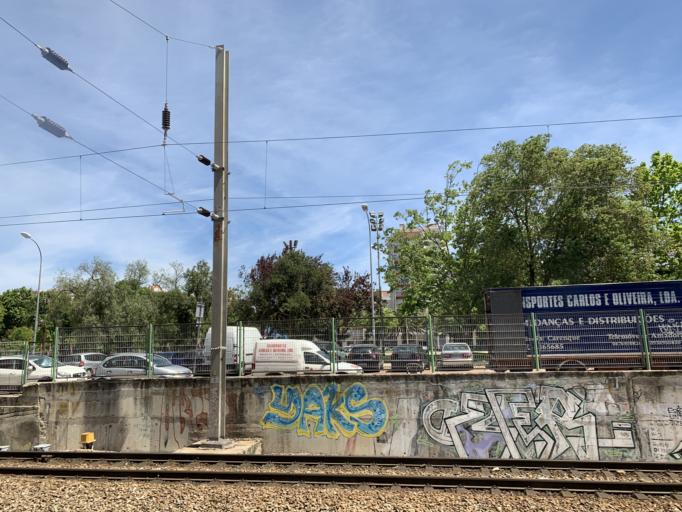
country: PT
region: Lisbon
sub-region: Amadora
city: Amadora
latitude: 38.7591
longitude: -9.2343
